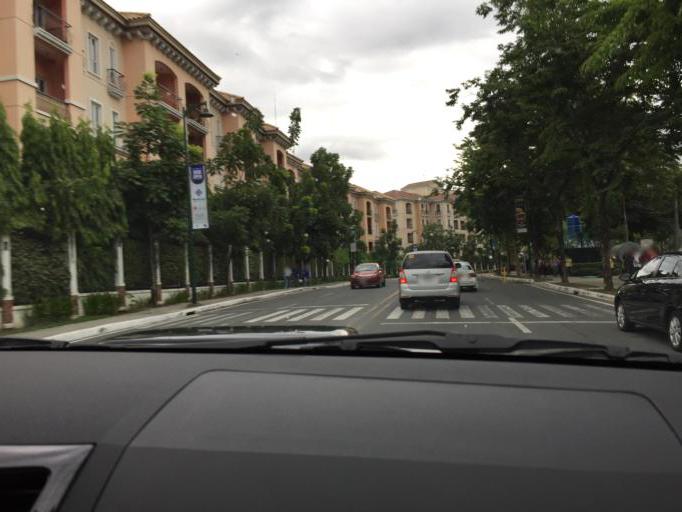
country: PH
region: Calabarzon
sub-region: Province of Rizal
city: Pateros
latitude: 14.5395
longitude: 121.0540
